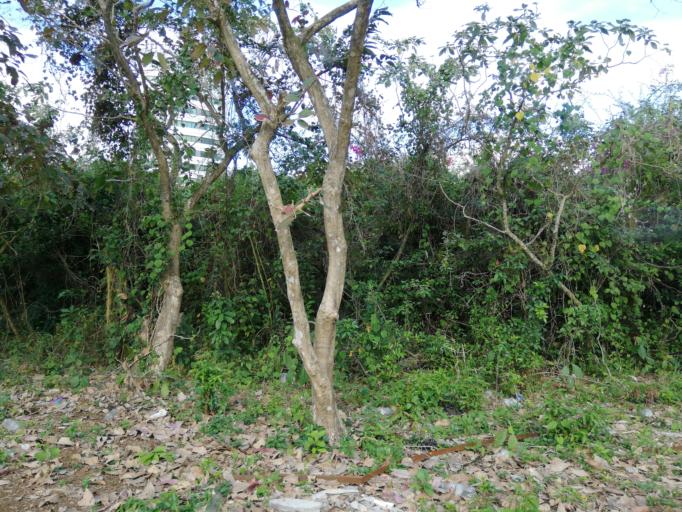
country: MU
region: Plaines Wilhems
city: Ebene
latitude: -20.2447
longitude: 57.4859
